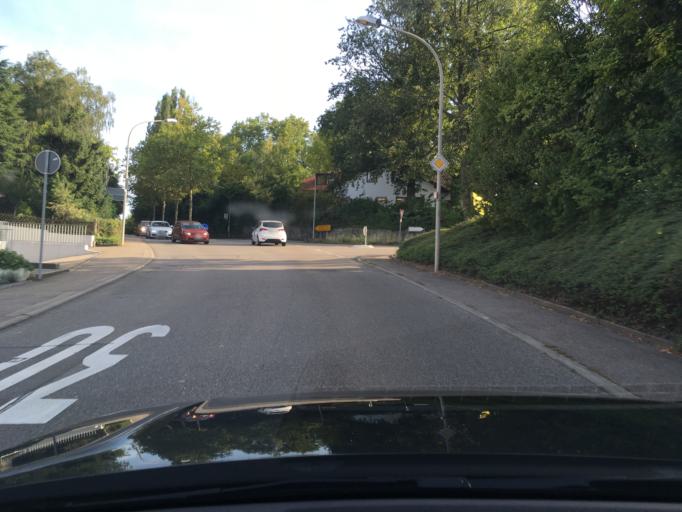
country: DE
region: Baden-Wuerttemberg
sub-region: Regierungsbezirk Stuttgart
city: Erdmannhausen
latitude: 48.9376
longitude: 9.2980
